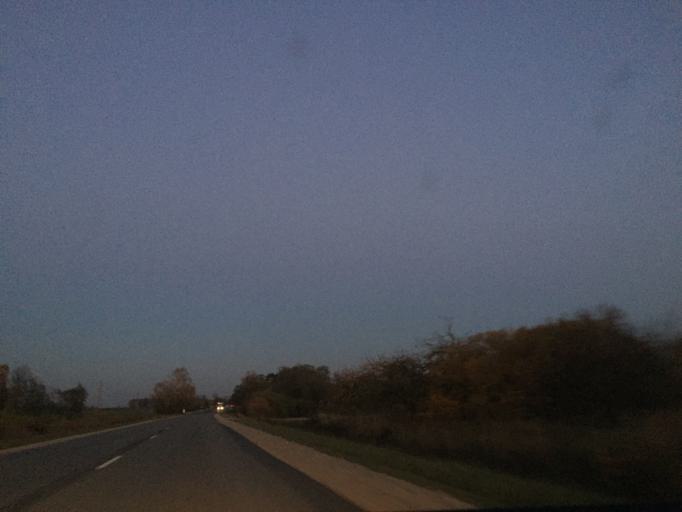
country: LT
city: Zagare
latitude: 56.4829
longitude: 23.1563
